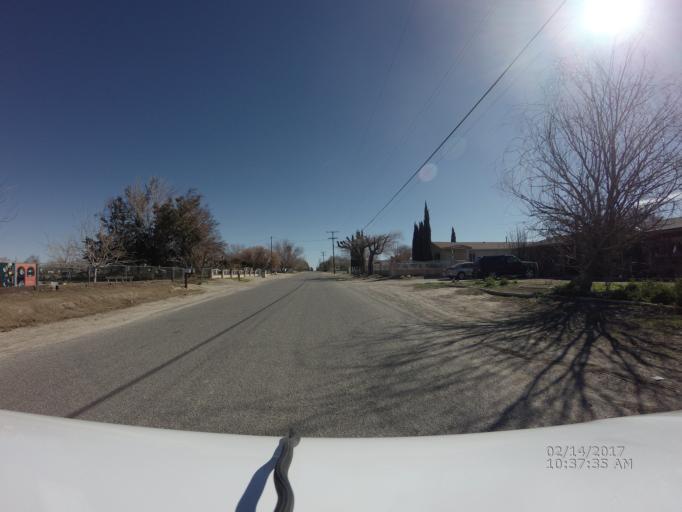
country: US
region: California
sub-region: Los Angeles County
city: Littlerock
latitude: 34.5634
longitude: -117.9464
